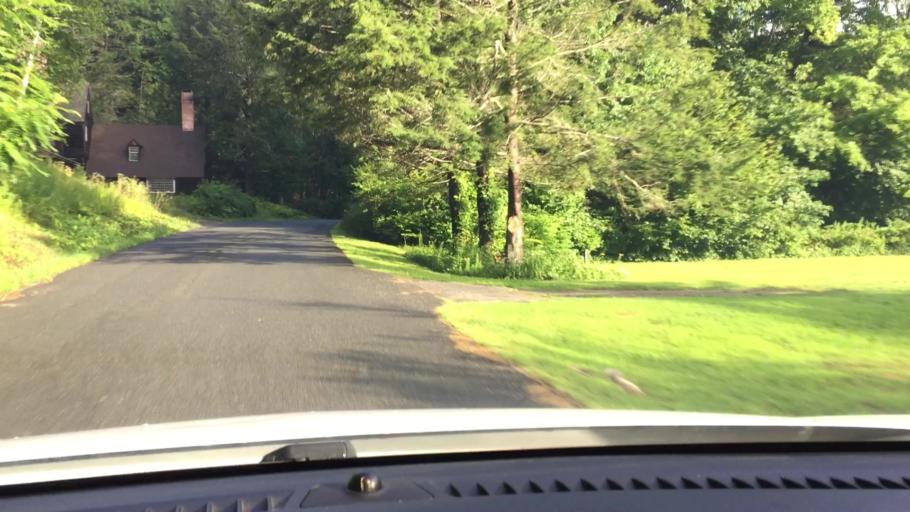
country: US
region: Massachusetts
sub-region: Berkshire County
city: Becket
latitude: 42.3640
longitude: -72.9688
